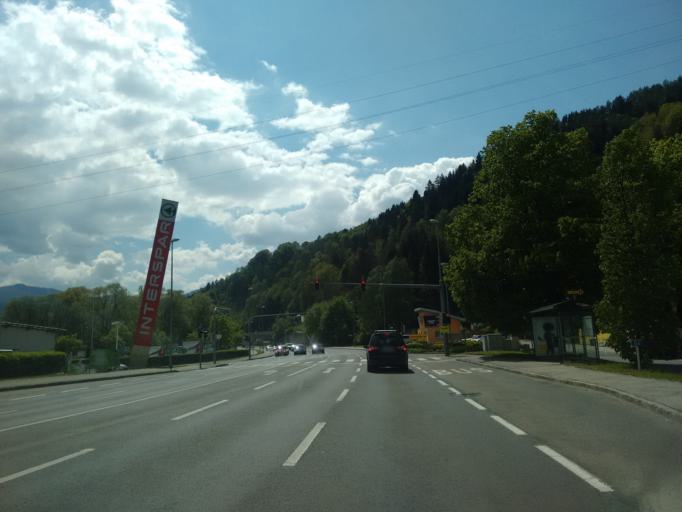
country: AT
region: Styria
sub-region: Politischer Bezirk Bruck-Muerzzuschlag
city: Bruck an der Mur
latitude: 47.4327
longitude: 15.2702
